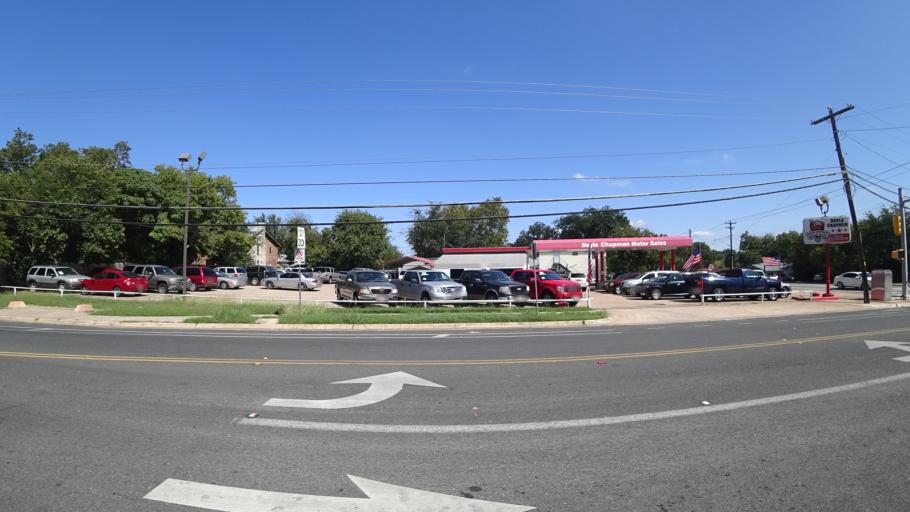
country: US
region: Texas
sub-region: Travis County
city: Austin
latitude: 30.3174
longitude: -97.7000
